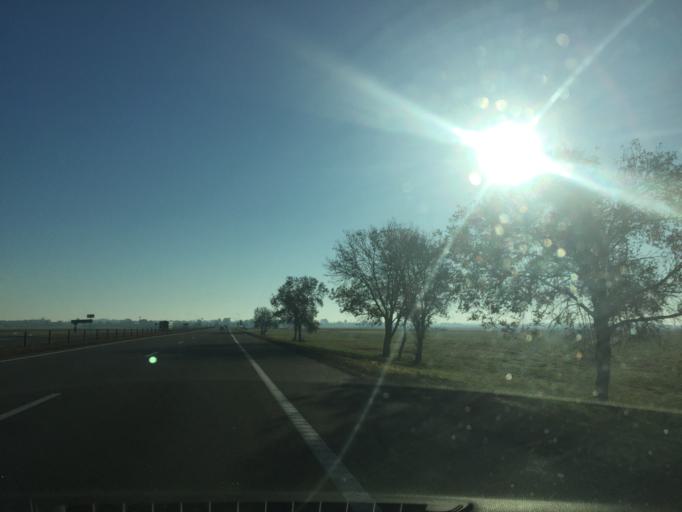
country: BY
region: Minsk
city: Smilavichy
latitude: 53.7599
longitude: 27.9508
